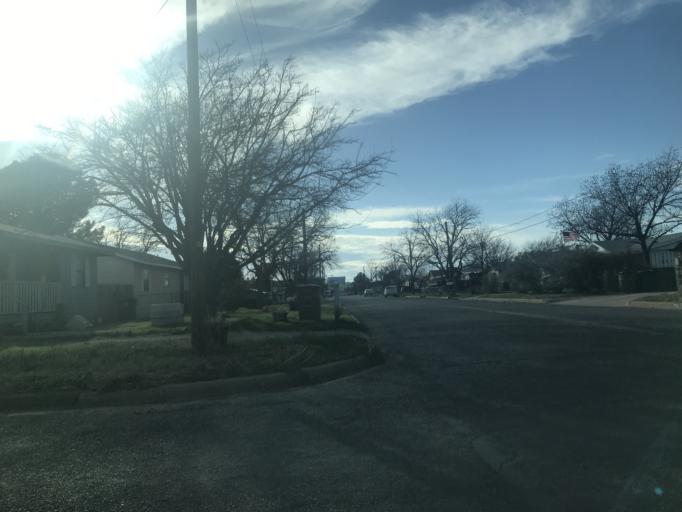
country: US
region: Texas
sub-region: Tom Green County
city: San Angelo
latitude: 31.4300
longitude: -100.4450
